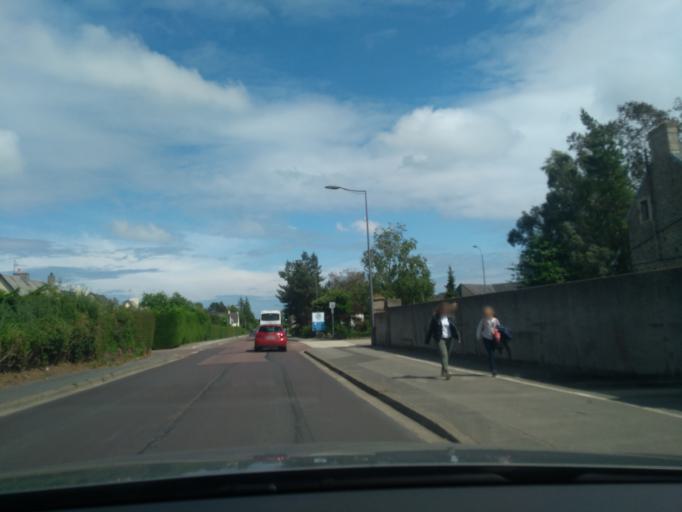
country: FR
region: Lower Normandy
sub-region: Departement de la Manche
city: Quettehou
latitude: 49.5921
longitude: -1.2999
